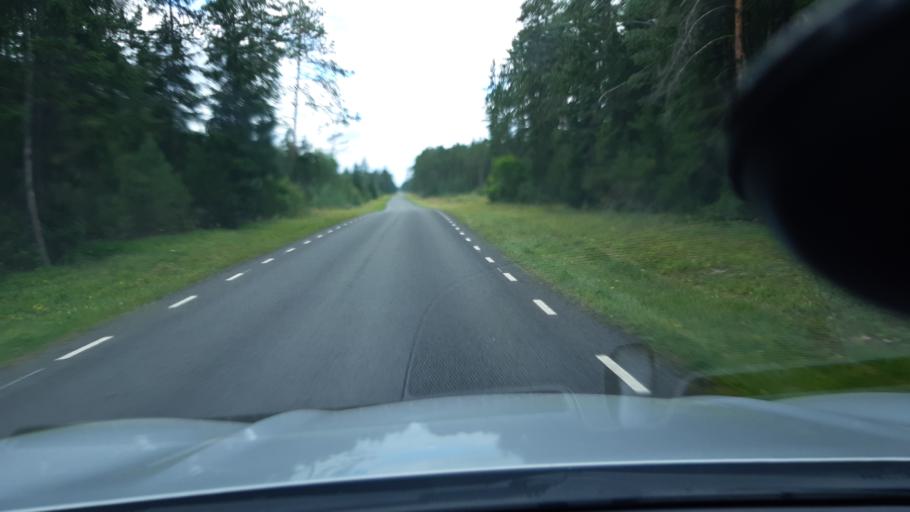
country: EE
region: Raplamaa
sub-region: Rapla vald
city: Rapla
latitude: 58.8922
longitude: 24.7111
